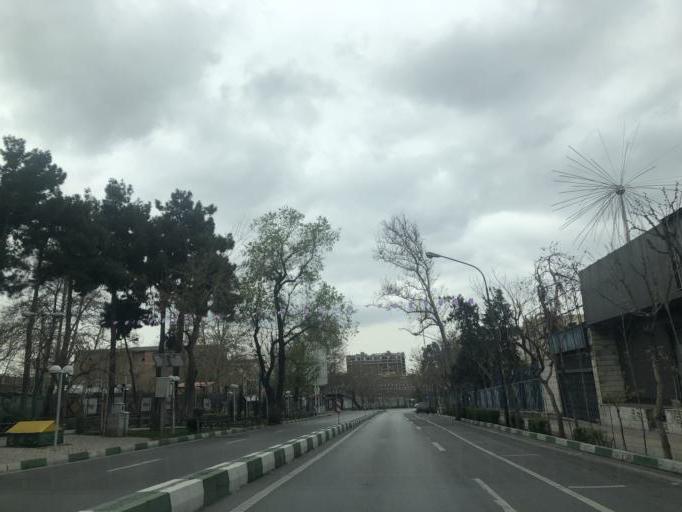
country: IR
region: Tehran
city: Tajrish
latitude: 35.7792
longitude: 51.4671
